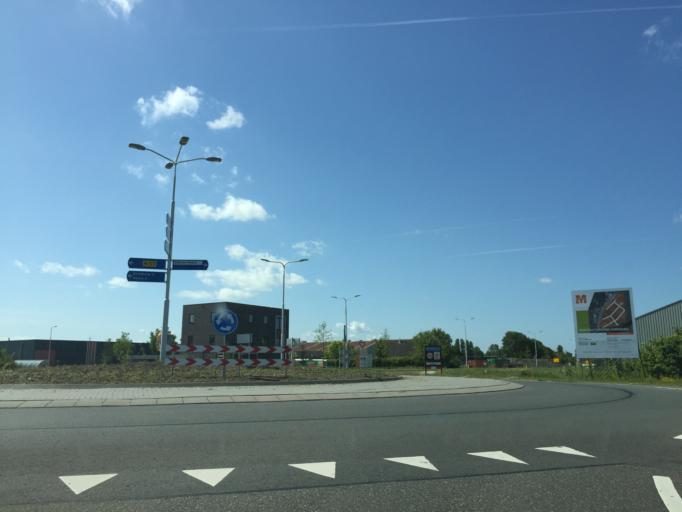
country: NL
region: Zeeland
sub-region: Gemeente Middelburg
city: Middelburg
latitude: 51.5056
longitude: 3.6311
